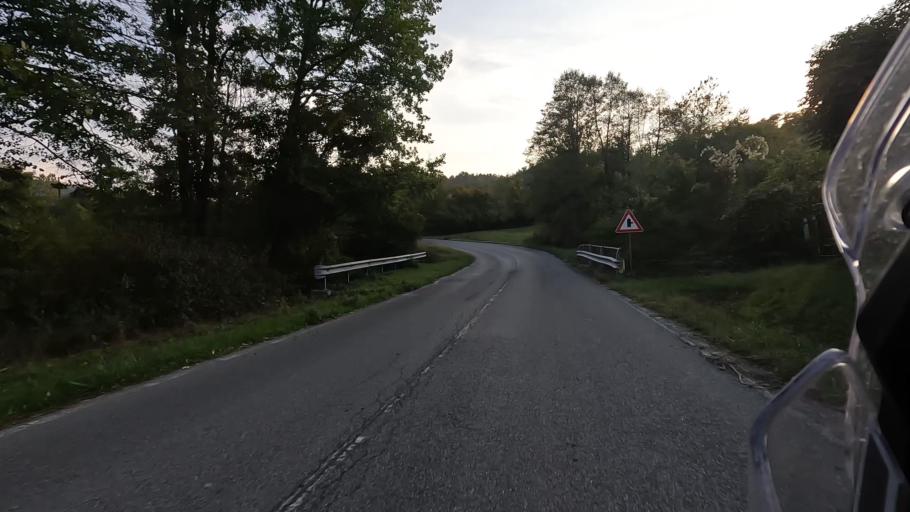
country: IT
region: Liguria
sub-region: Provincia di Savona
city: Mioglia
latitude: 44.5094
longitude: 8.4364
